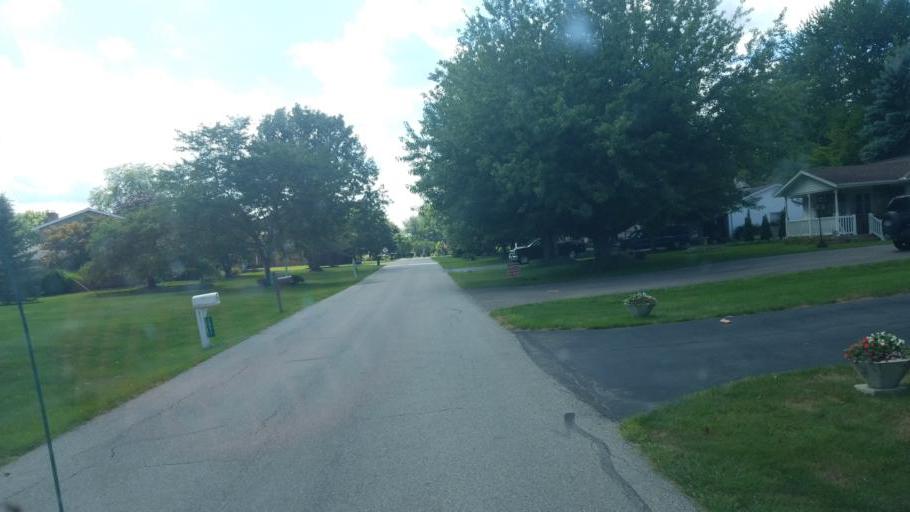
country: US
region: Ohio
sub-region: Marion County
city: Marion
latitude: 40.5323
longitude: -83.0927
